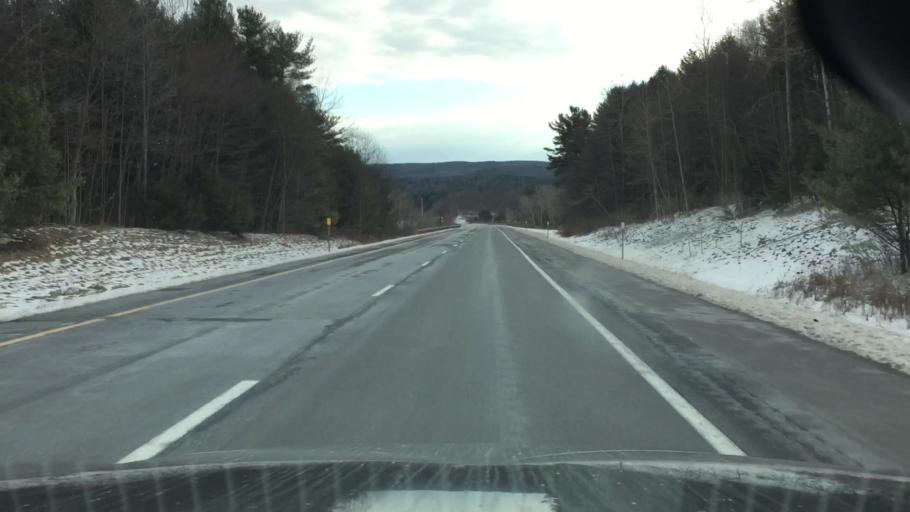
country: US
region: New York
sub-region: Chenango County
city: Bainbridge
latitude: 42.1974
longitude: -75.5488
